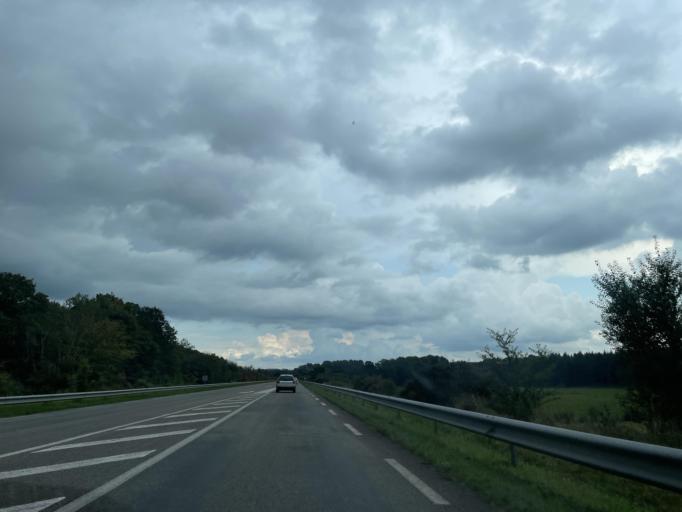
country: FR
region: Haute-Normandie
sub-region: Departement de la Seine-Maritime
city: Forges-les-Eaux
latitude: 49.6013
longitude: 1.5527
